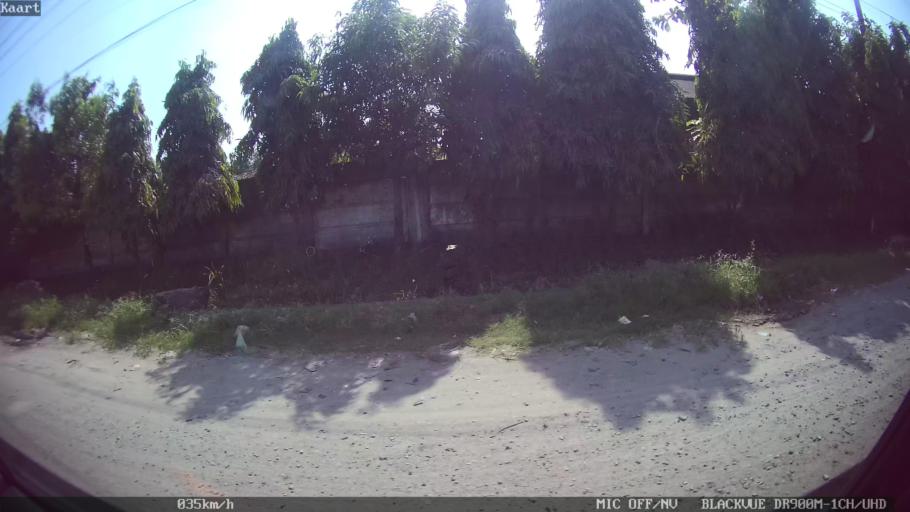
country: ID
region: Lampung
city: Natar
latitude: -5.2639
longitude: 105.1854
